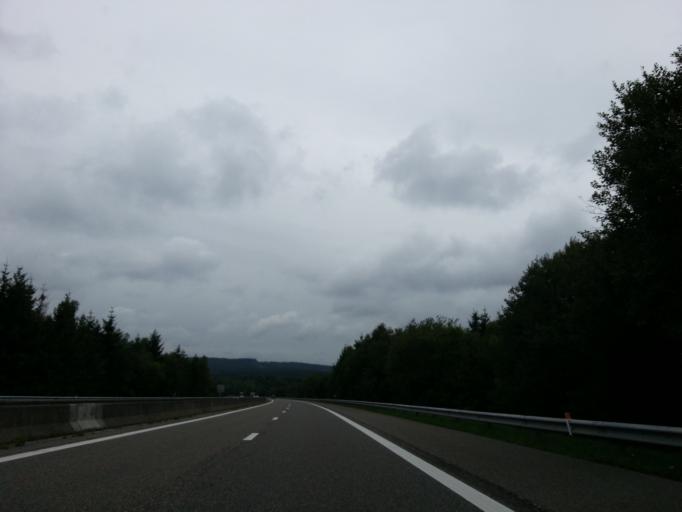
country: BE
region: Wallonia
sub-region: Province de Liege
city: Saint-Vith
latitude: 50.3272
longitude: 6.0902
